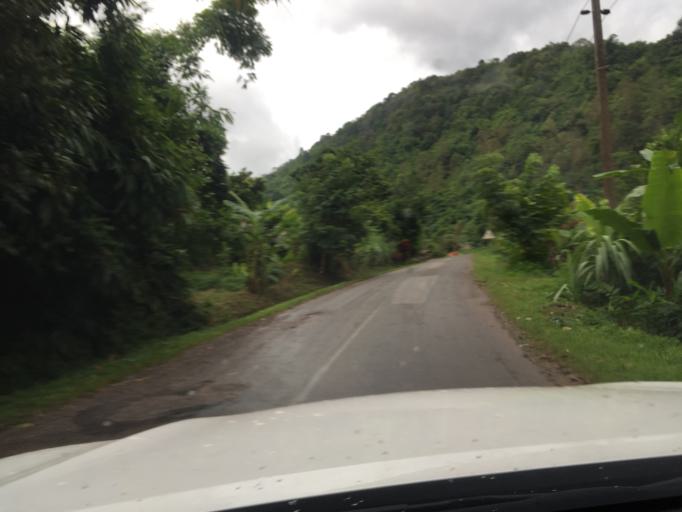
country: LA
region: Oudomxai
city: Muang La
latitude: 20.8156
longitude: 102.0928
